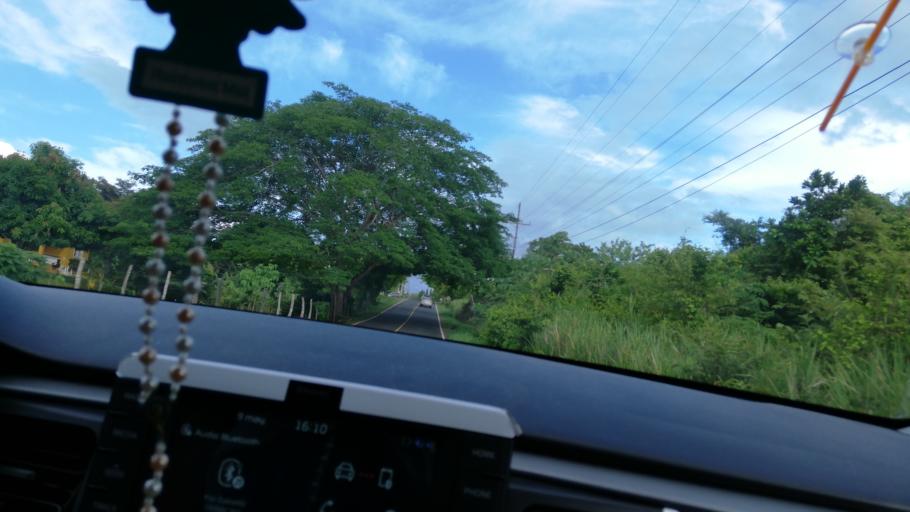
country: PA
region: Panama
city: Las Colinas
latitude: 8.4865
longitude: -80.0213
